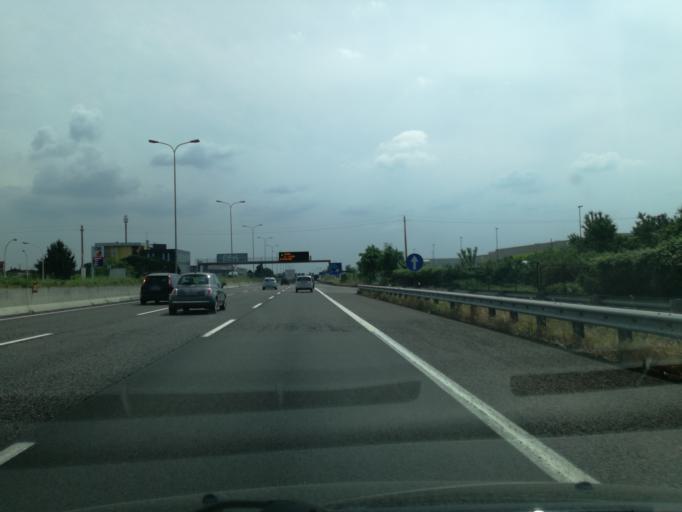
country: IT
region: Lombardy
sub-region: Provincia di Monza e Brianza
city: Verano Brianza
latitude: 45.6751
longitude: 9.2191
